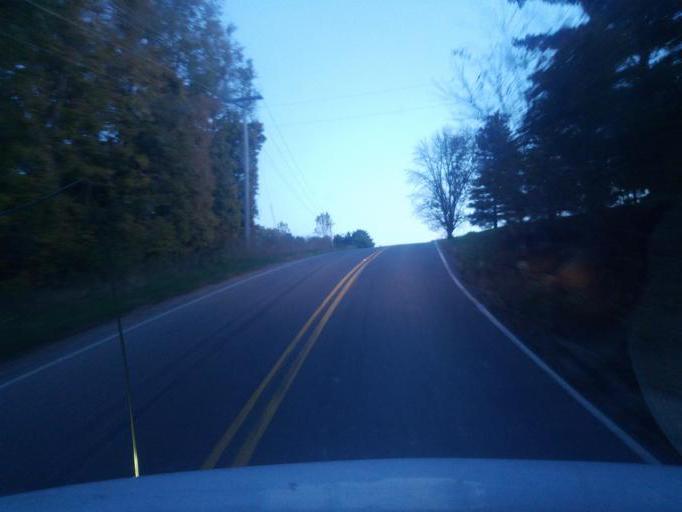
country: US
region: Ohio
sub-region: Perry County
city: Somerset
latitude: 39.8693
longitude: -82.2517
